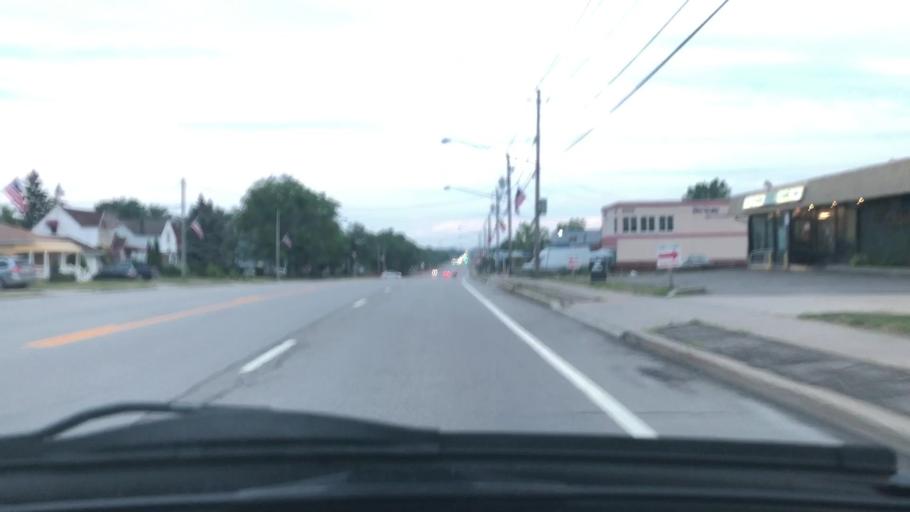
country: US
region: New York
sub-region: Erie County
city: Sloan
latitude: 42.9083
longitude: -78.7842
